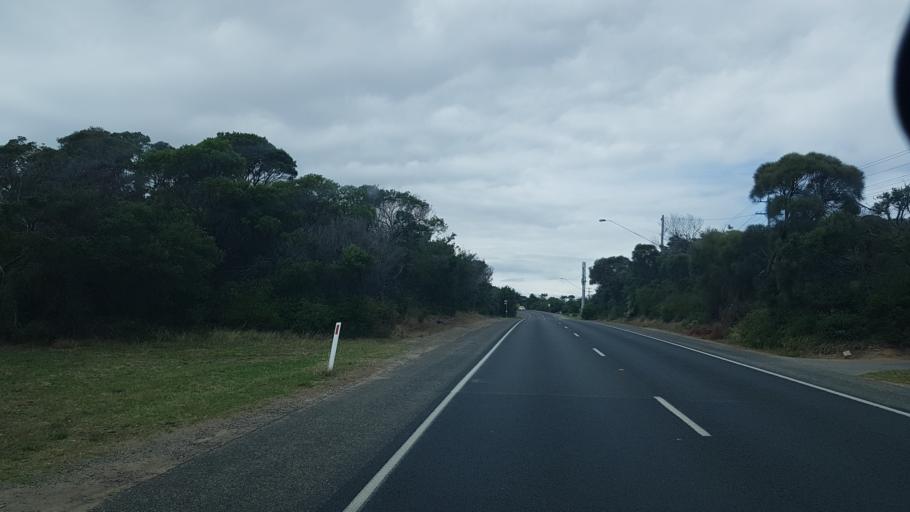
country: AU
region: Victoria
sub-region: Mornington Peninsula
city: Sorrento
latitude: -38.3540
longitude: 144.7512
